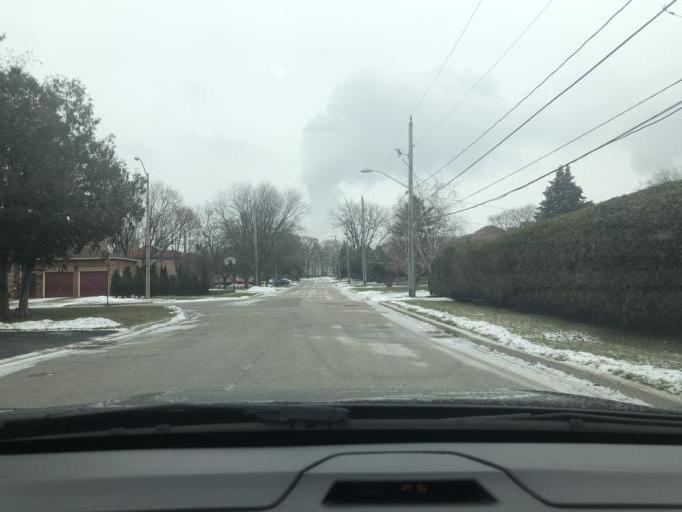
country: CA
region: Ontario
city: Scarborough
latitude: 43.7821
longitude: -79.2696
